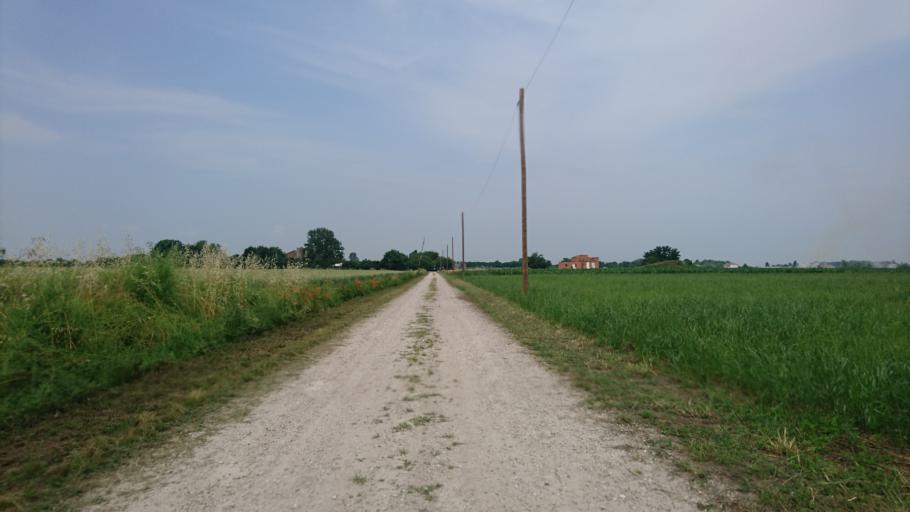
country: IT
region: Veneto
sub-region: Provincia di Padova
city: Polverara
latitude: 45.3251
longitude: 11.9531
